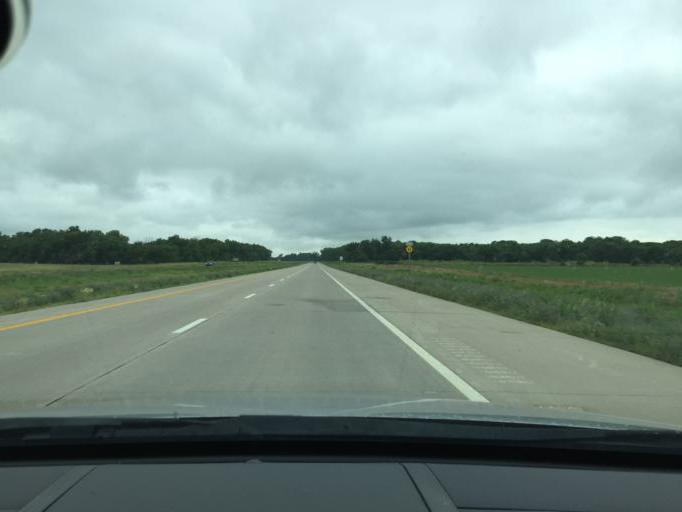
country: US
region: Kansas
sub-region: Reno County
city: Buhler
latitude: 38.1511
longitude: -97.8551
